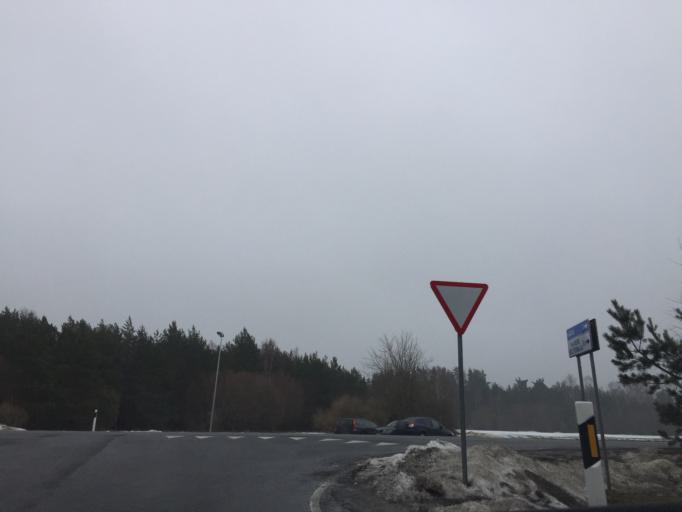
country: EE
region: Saare
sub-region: Kuressaare linn
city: Kuressaare
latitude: 58.2654
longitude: 22.5915
